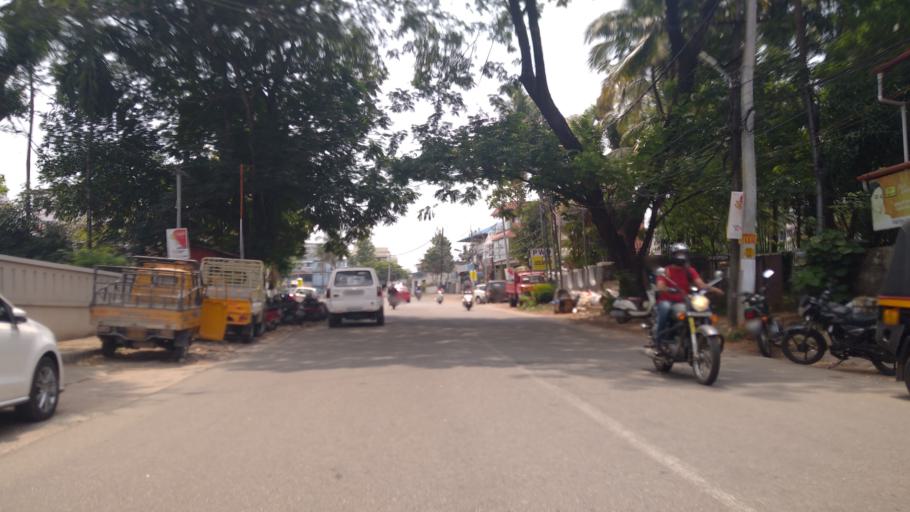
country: IN
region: Kerala
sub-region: Ernakulam
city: Elur
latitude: 10.0321
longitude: 76.3225
